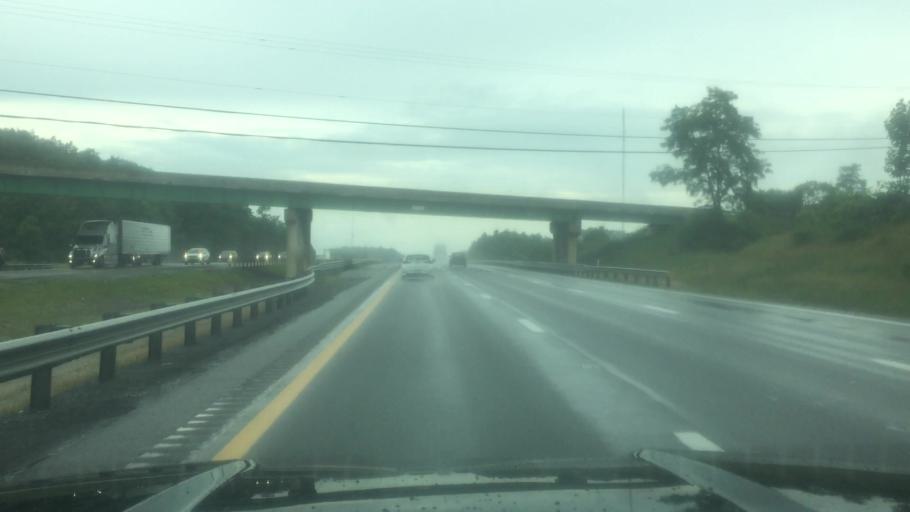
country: US
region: West Virginia
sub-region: Raleigh County
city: Shady Spring
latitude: 37.5804
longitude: -81.1177
